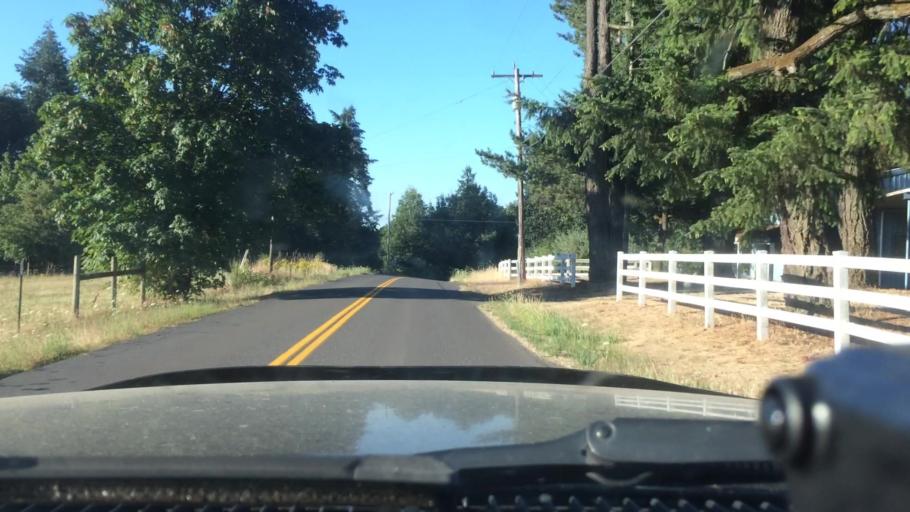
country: US
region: Oregon
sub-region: Yamhill County
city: Newberg
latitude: 45.3216
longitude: -122.9404
